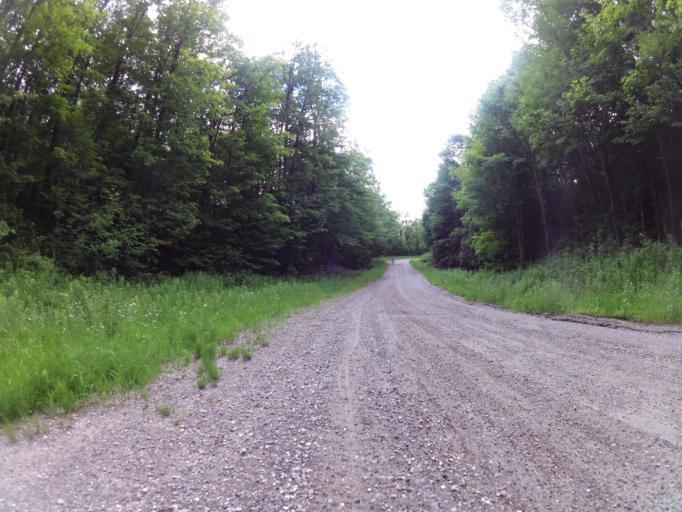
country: CA
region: Ontario
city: Renfrew
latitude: 45.0444
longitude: -76.7432
